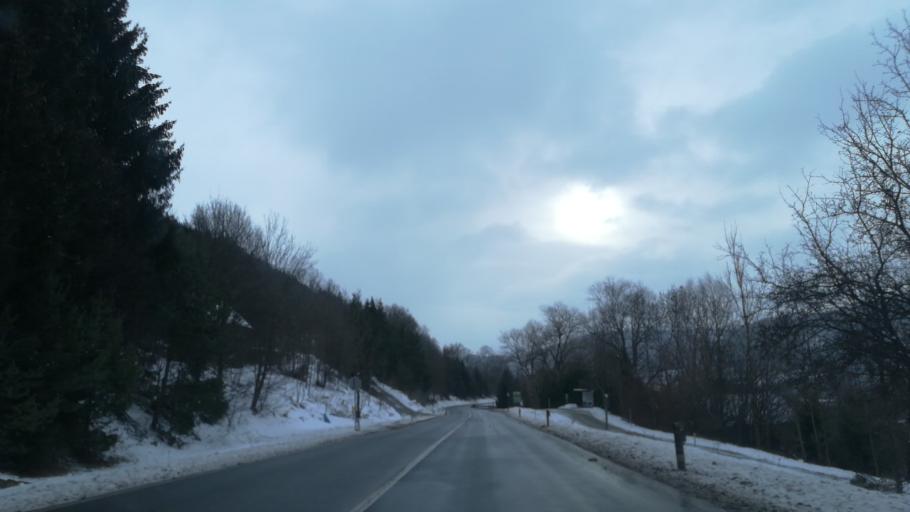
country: AT
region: Styria
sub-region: Politischer Bezirk Murtal
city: Poels
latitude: 47.2067
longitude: 14.5824
